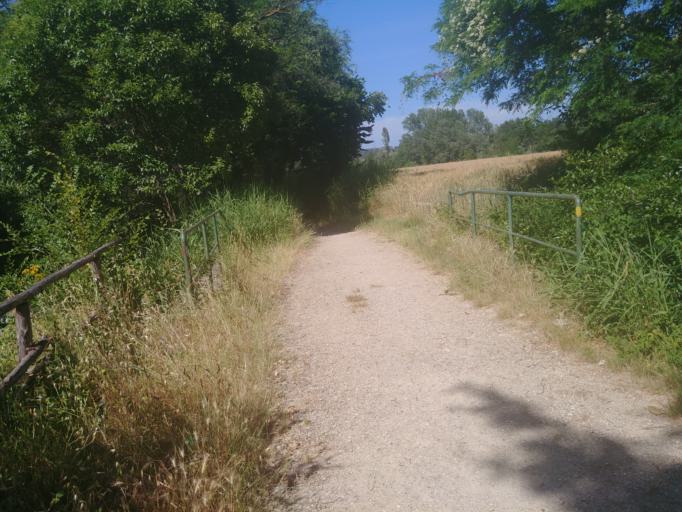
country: IT
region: Umbria
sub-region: Provincia di Perugia
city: Ponte Felcino
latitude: 43.1376
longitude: 12.4524
